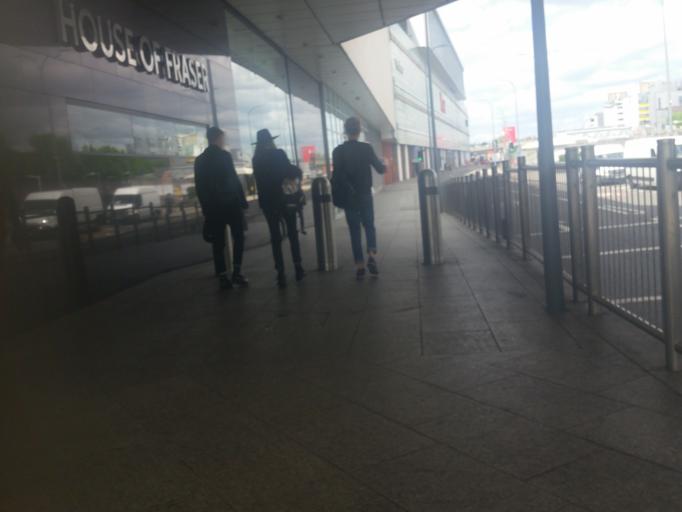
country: GB
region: England
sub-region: Greater London
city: Hammersmith
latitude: 51.5059
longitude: -0.2182
